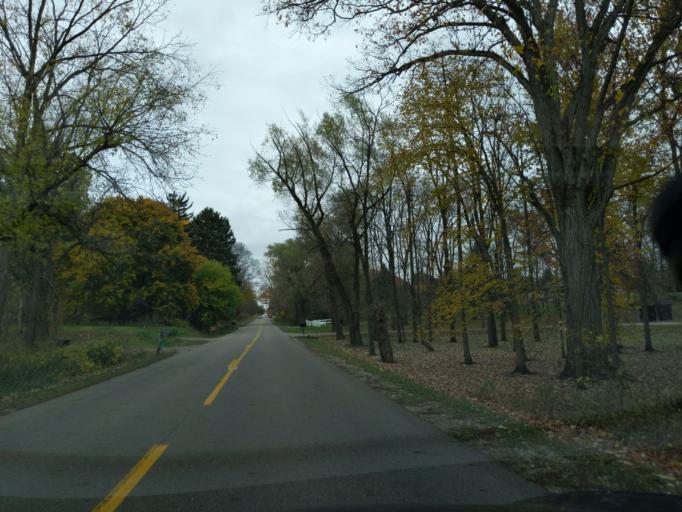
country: US
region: Michigan
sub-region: Eaton County
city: Eaton Rapids
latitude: 42.5241
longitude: -84.6057
